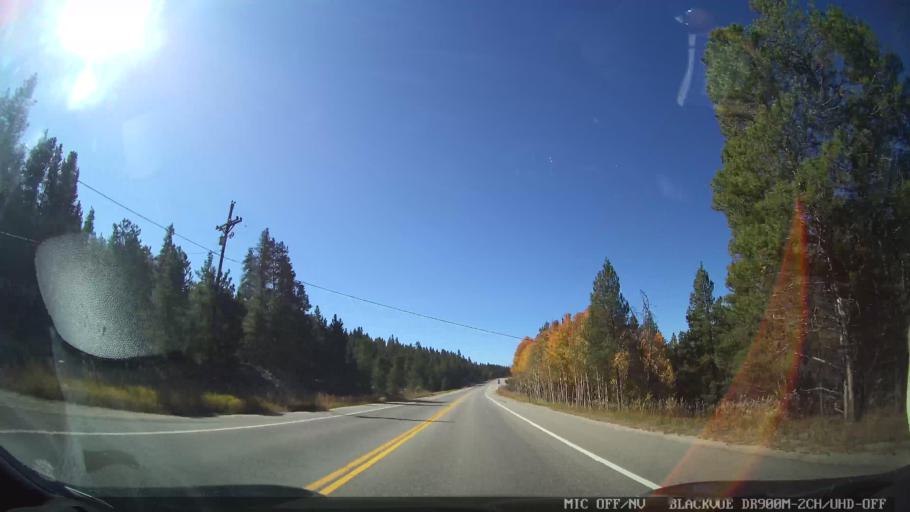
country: US
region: Colorado
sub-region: Lake County
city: Leadville North
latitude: 39.2770
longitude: -106.2830
